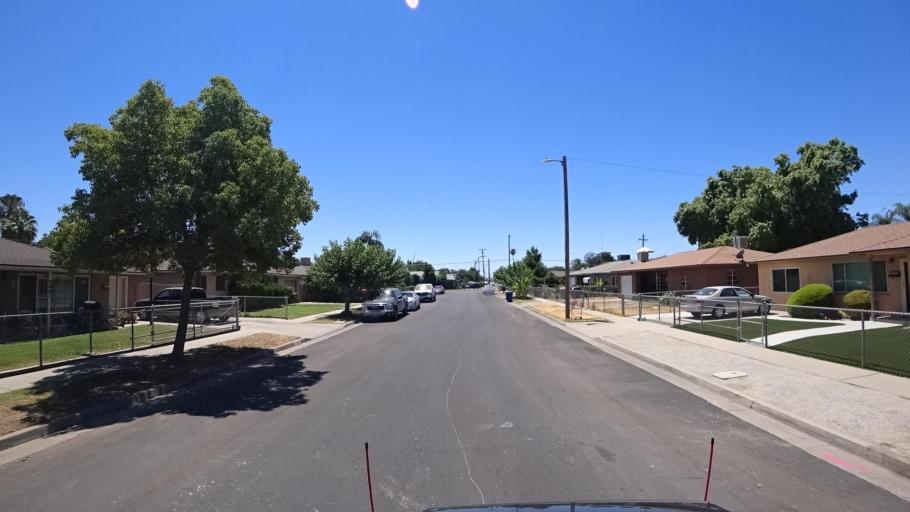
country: US
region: California
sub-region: Fresno County
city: Fresno
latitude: 36.7113
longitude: -119.7519
